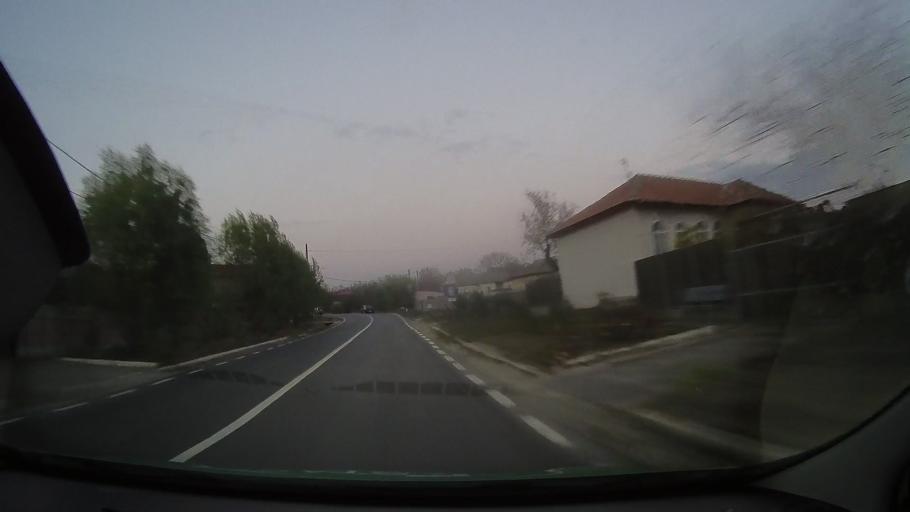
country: RO
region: Constanta
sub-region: Comuna Baneasa
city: Baneasa
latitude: 44.0634
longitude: 27.7039
